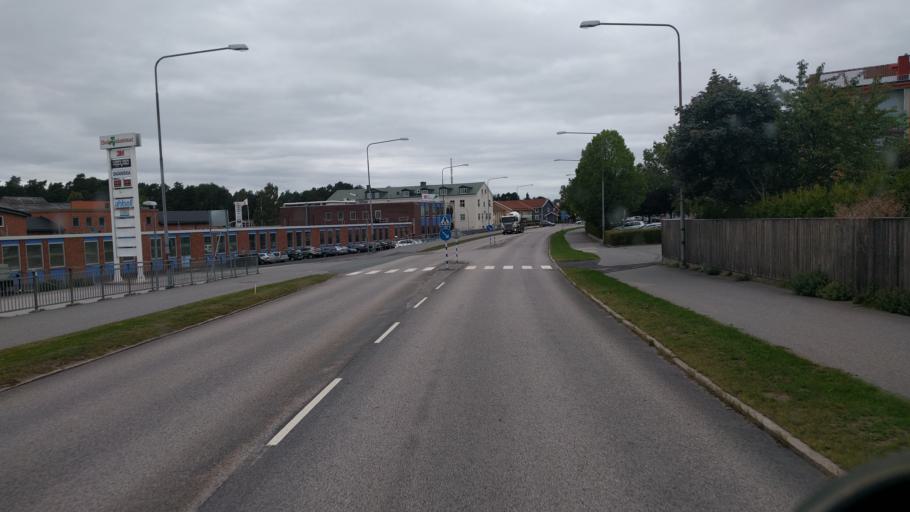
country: SE
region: Kalmar
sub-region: Vasterviks Kommun
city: Vaestervik
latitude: 57.7532
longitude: 16.6260
